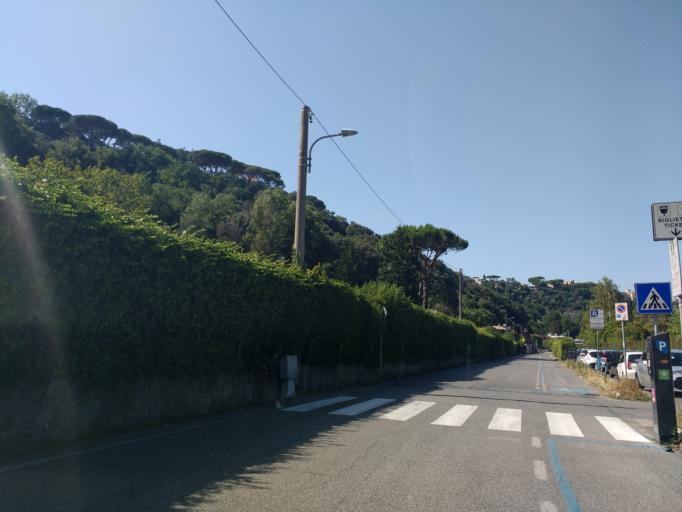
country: IT
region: Latium
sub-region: Citta metropolitana di Roma Capitale
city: Castel Gandolfo
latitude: 41.7522
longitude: 12.6512
